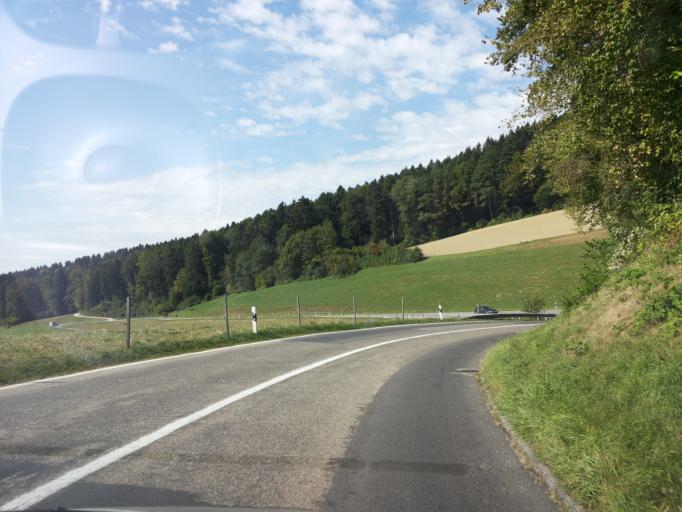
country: CH
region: Lucerne
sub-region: Willisau District
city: Pfaffnau
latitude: 47.2205
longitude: 7.8720
